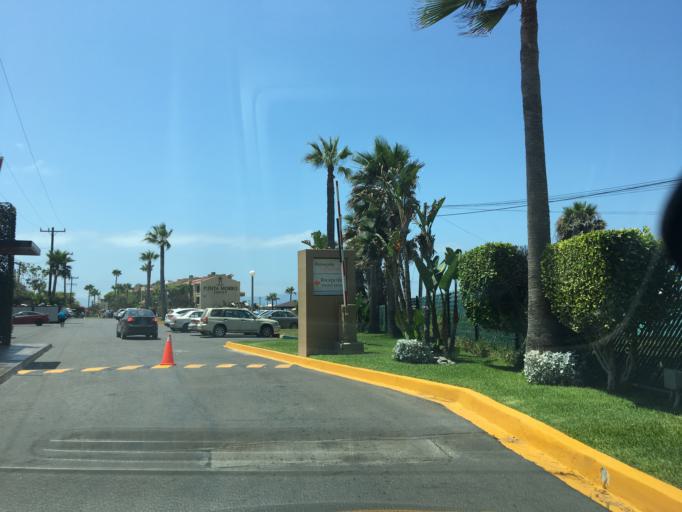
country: MX
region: Baja California
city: El Sauzal
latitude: 31.8645
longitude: -116.6687
